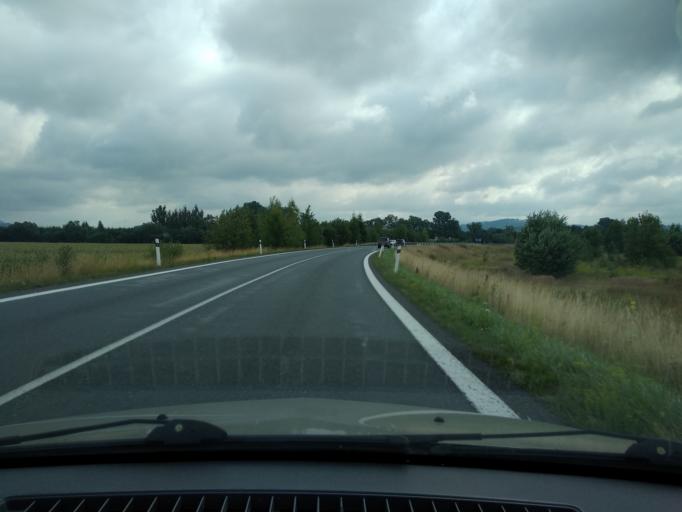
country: CZ
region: Olomoucky
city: Postrelmov
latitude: 49.9163
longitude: 16.9139
